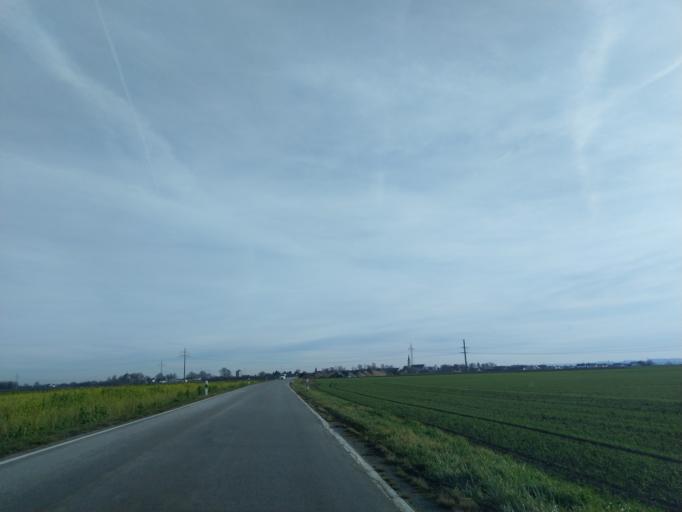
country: DE
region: Bavaria
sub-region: Lower Bavaria
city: Otzing
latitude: 48.7656
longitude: 12.7920
